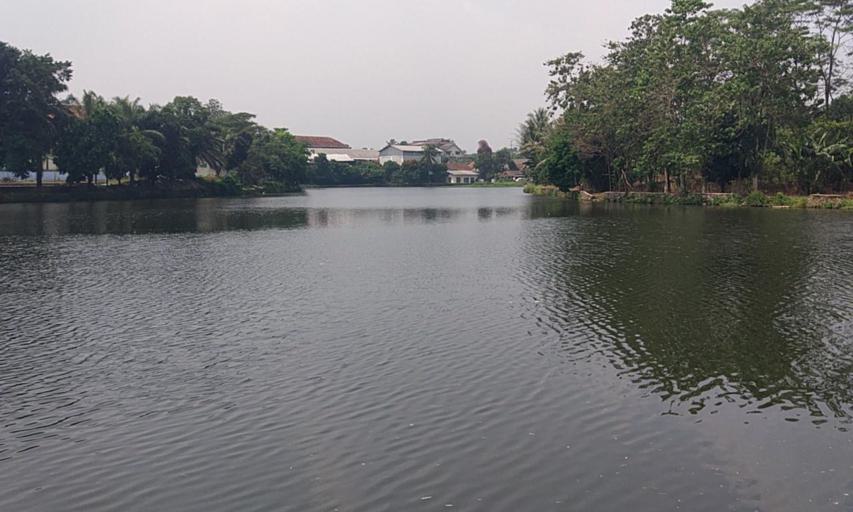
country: ID
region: West Java
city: Ciampea
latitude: -6.5229
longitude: 106.7573
